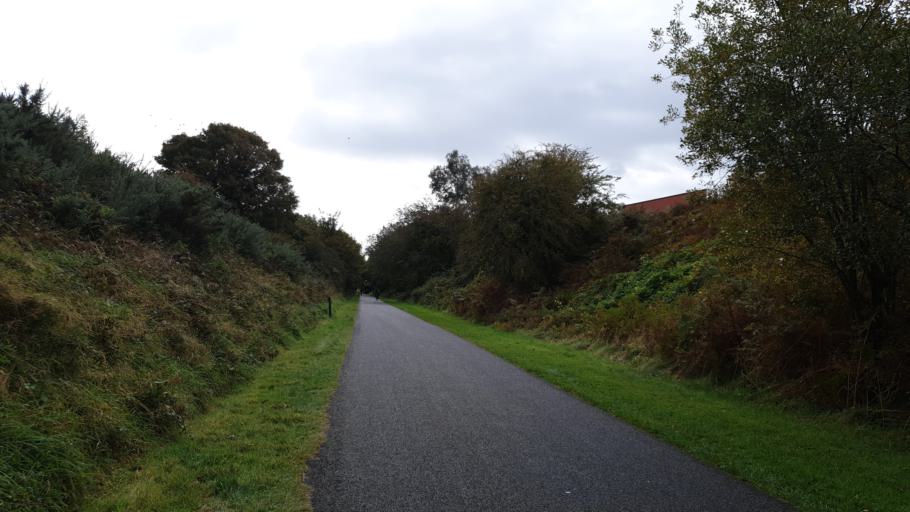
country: IE
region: Munster
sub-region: County Cork
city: Cork
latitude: 51.8925
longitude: -8.4142
